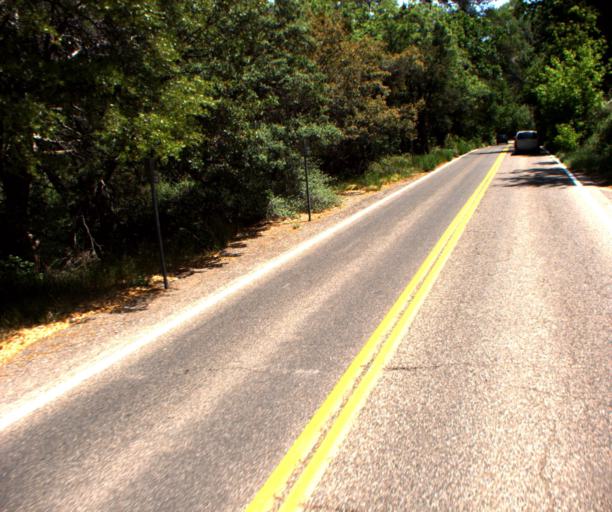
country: US
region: Arizona
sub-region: Coconino County
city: Sedona
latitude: 34.9378
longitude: -111.7481
